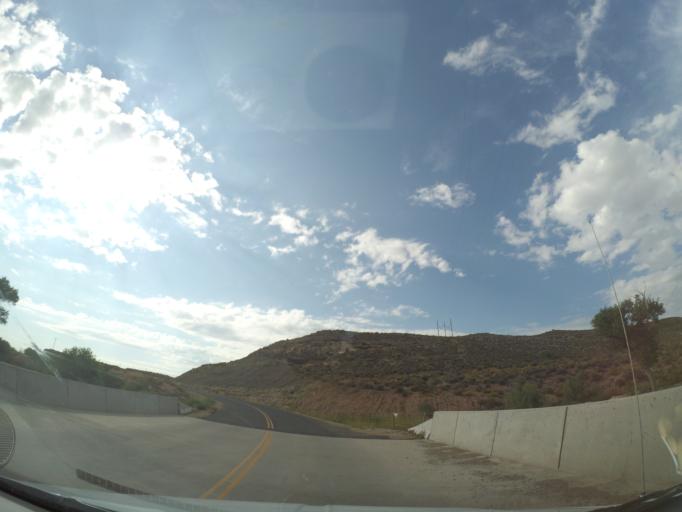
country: US
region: Utah
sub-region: Washington County
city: LaVerkin
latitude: 37.2050
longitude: -113.1715
